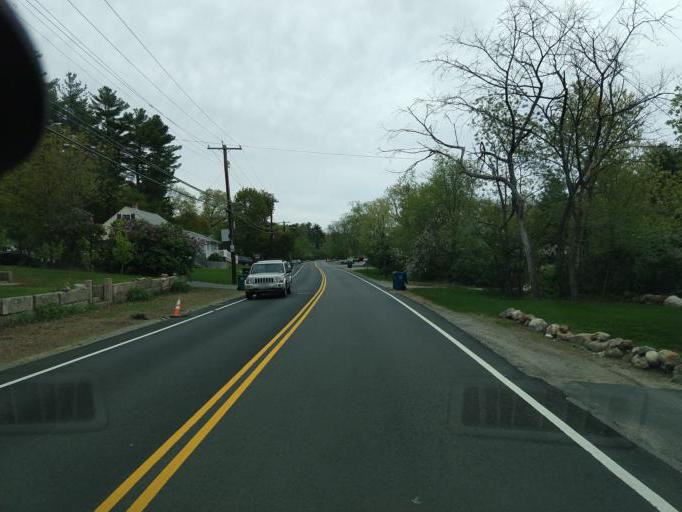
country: US
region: Massachusetts
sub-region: Middlesex County
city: Billerica
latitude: 42.5705
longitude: -71.2451
